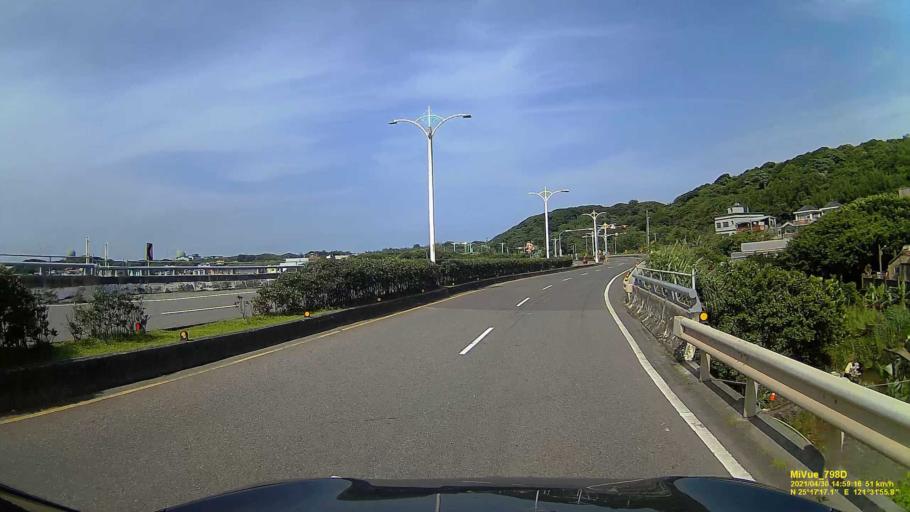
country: TW
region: Taipei
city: Taipei
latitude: 25.2882
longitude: 121.5325
